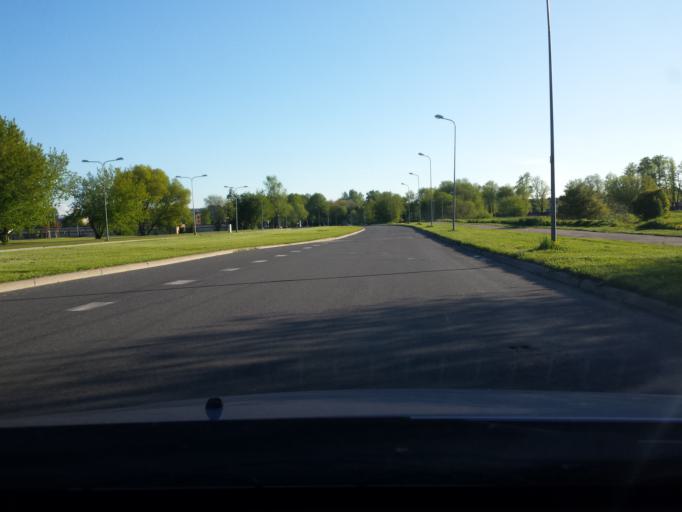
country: LV
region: Riga
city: Jaunciems
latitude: 56.9932
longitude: 24.1693
